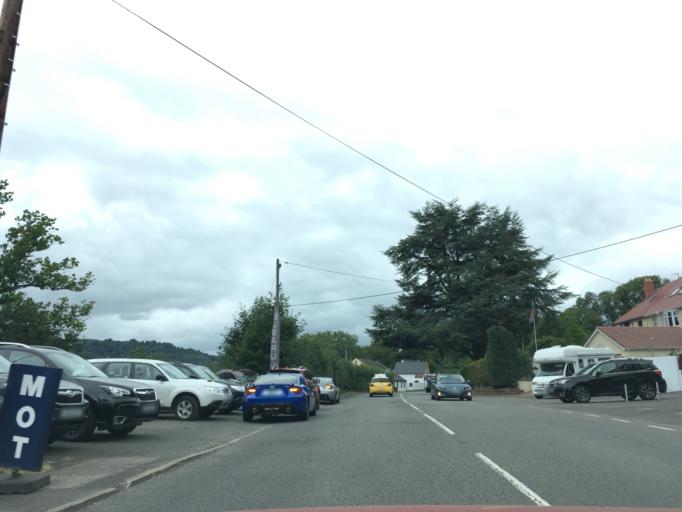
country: GB
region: Wales
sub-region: Monmouthshire
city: Gilwern
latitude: 51.8379
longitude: -3.0832
